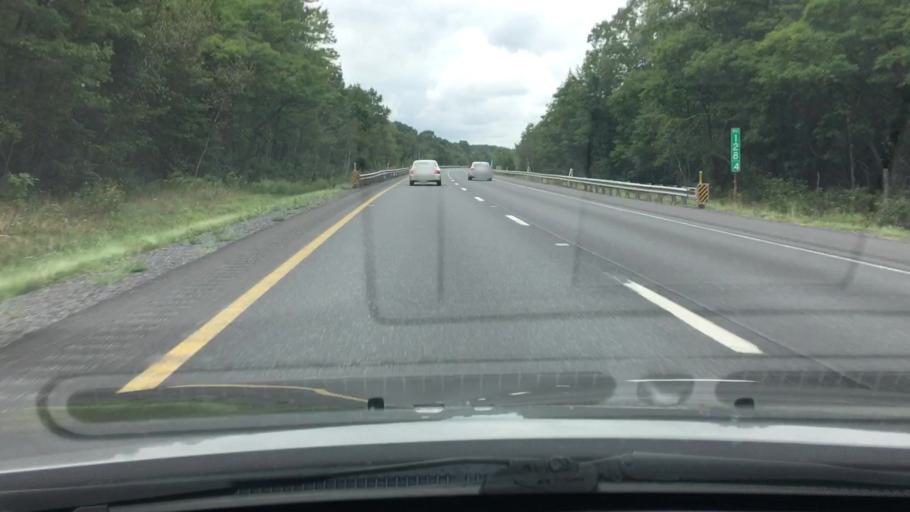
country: US
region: Pennsylvania
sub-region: Schuylkill County
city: Mahanoy City
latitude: 40.7892
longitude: -76.1442
